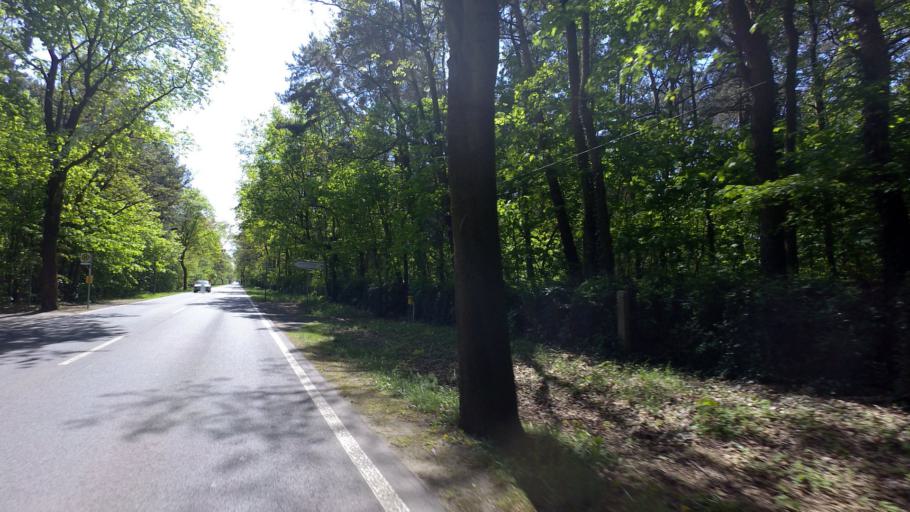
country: DE
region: Brandenburg
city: Bestensee
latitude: 52.2553
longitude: 13.6544
